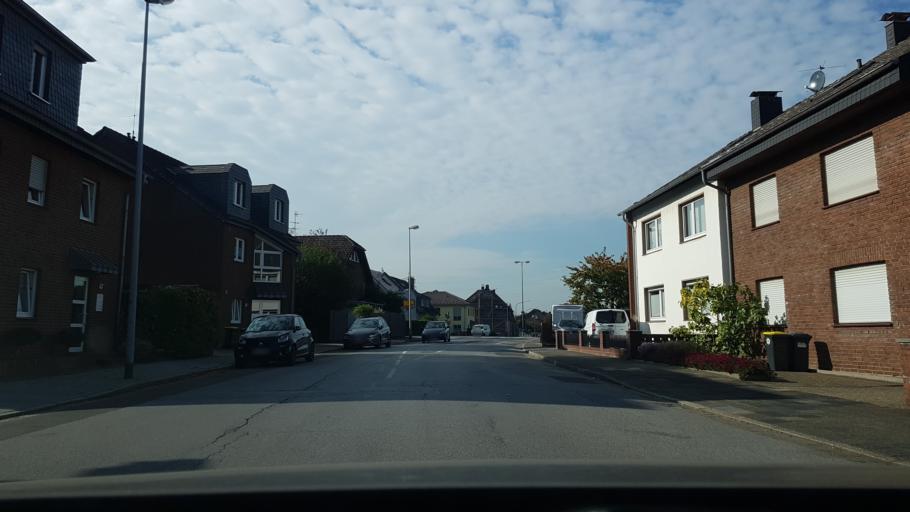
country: DE
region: North Rhine-Westphalia
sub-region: Regierungsbezirk Dusseldorf
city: Moers
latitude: 51.4196
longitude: 6.6660
